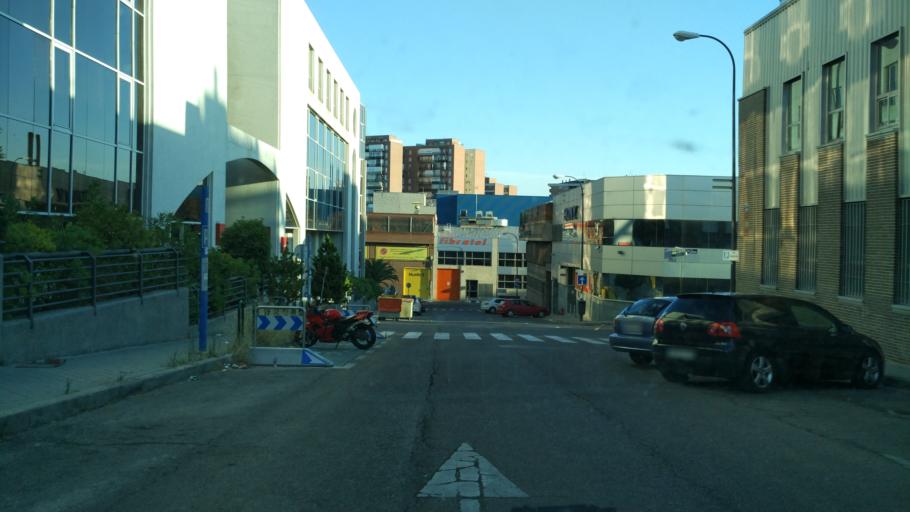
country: ES
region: Madrid
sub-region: Provincia de Madrid
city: Las Tablas
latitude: 40.4904
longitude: -3.6903
